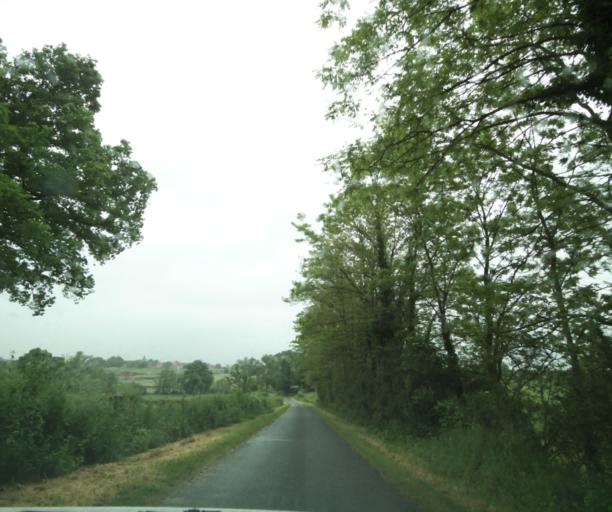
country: FR
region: Bourgogne
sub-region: Departement de Saone-et-Loire
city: Palinges
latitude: 46.4871
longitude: 4.1916
